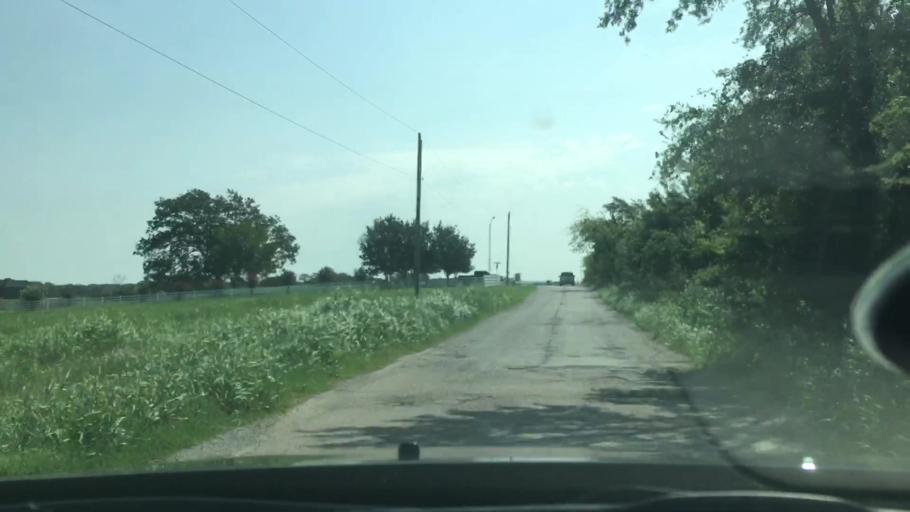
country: US
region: Oklahoma
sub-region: Bryan County
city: Durant
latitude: 34.0556
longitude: -96.3656
